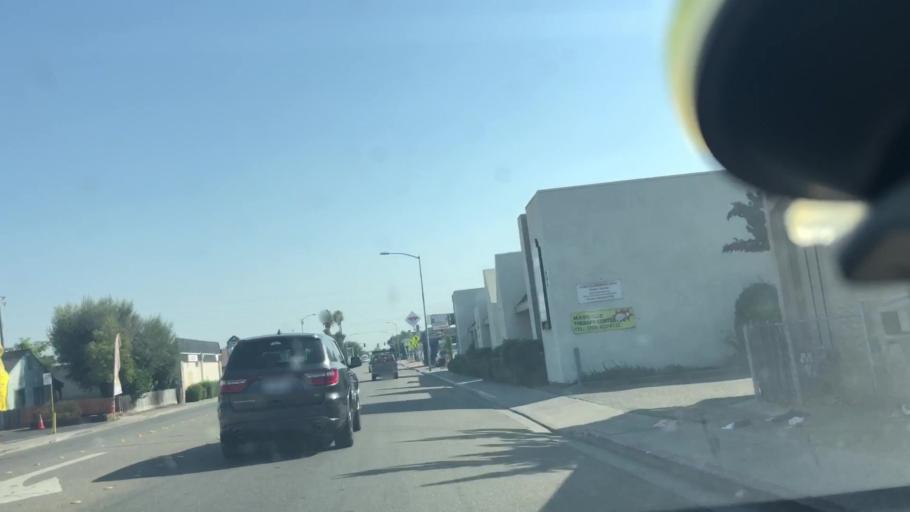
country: US
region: California
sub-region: San Joaquin County
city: Manteca
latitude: 37.8037
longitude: -121.2168
